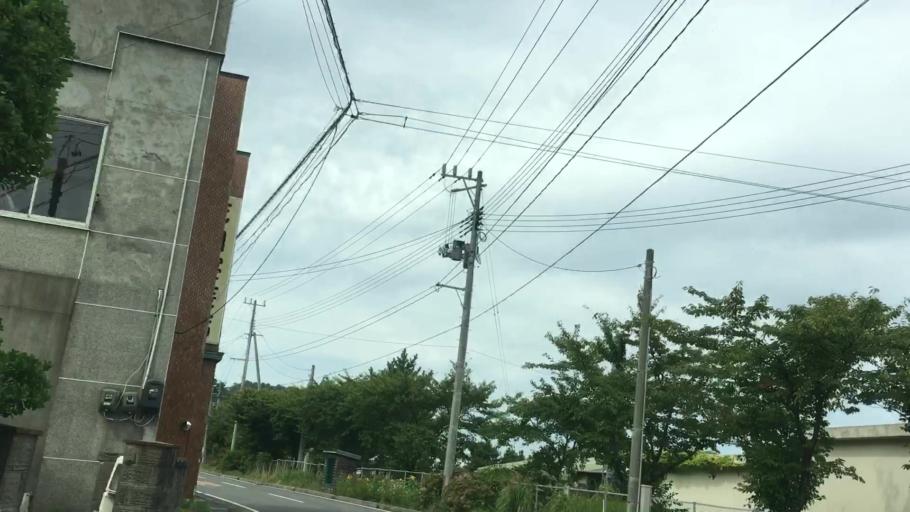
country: JP
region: Aomori
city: Shimokizukuri
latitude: 40.7781
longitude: 140.2128
